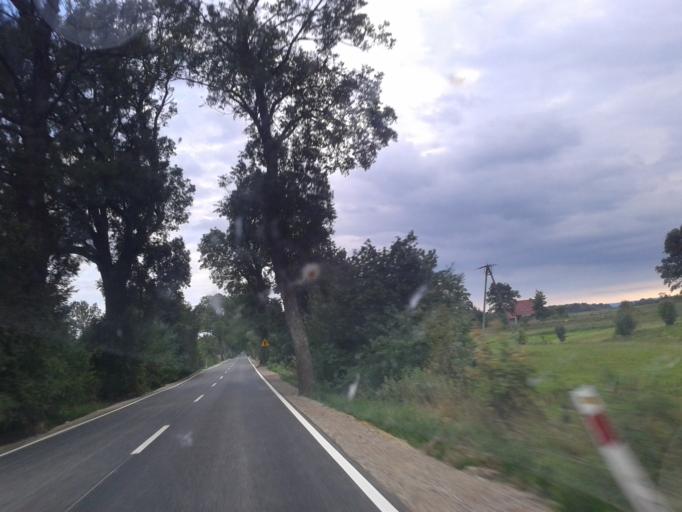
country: PL
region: West Pomeranian Voivodeship
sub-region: Powiat szczecinecki
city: Grzmiaca
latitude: 53.8665
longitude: 16.4834
